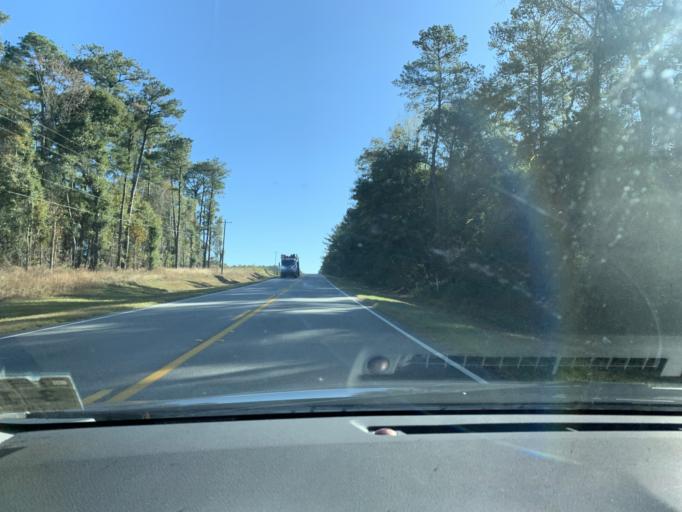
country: US
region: Georgia
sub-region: Coffee County
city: Broxton
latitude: 31.7719
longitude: -83.0429
